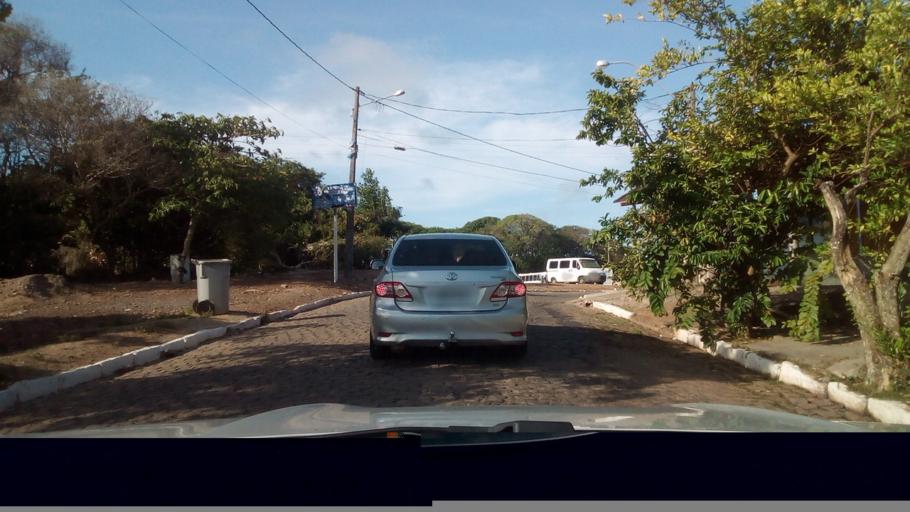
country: BR
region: Paraiba
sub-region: Joao Pessoa
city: Joao Pessoa
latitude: -7.1658
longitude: -34.7994
